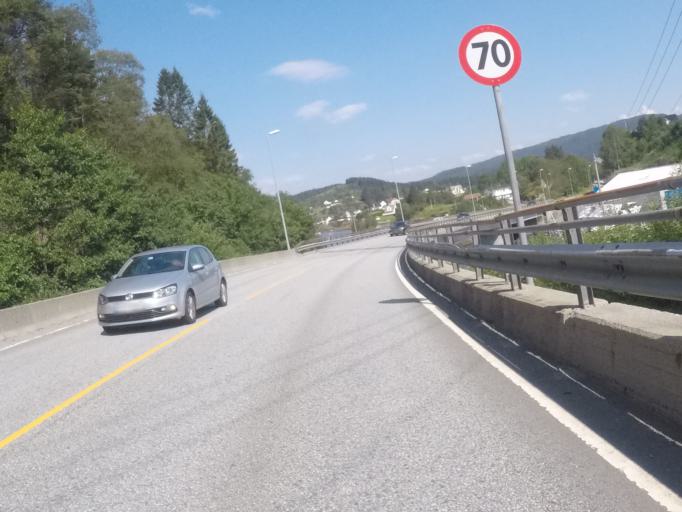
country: NO
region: Hordaland
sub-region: Bergen
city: Hylkje
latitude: 60.6027
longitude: 5.3970
